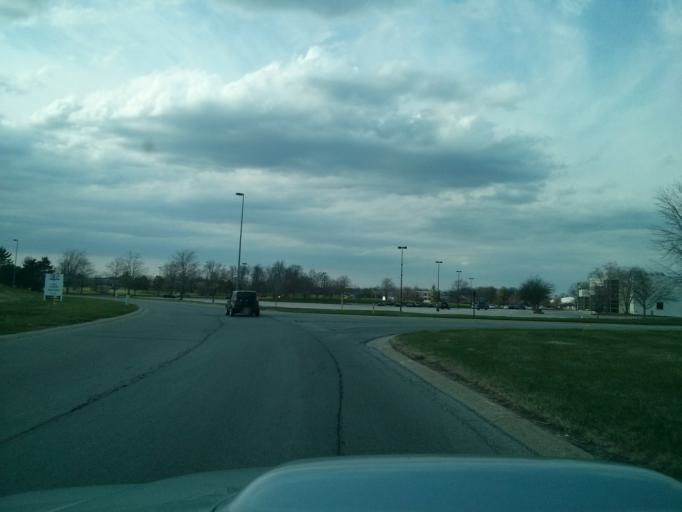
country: US
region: Indiana
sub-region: Hamilton County
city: Carmel
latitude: 39.9597
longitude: -86.1459
